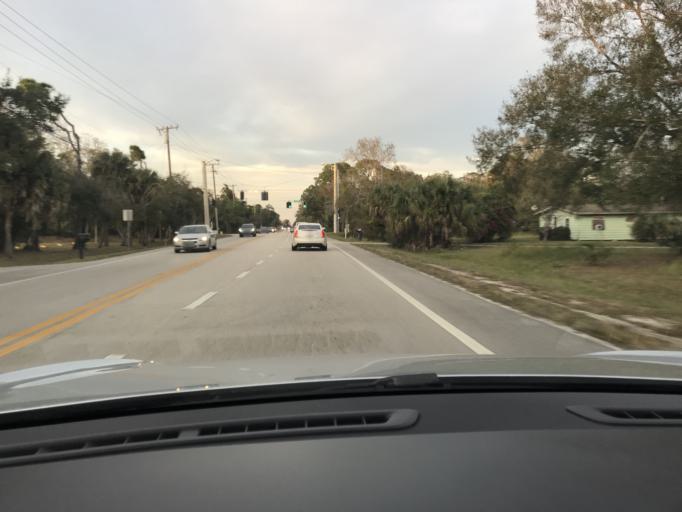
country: US
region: Florida
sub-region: Indian River County
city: Vero Beach South
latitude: 27.6083
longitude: -80.4305
